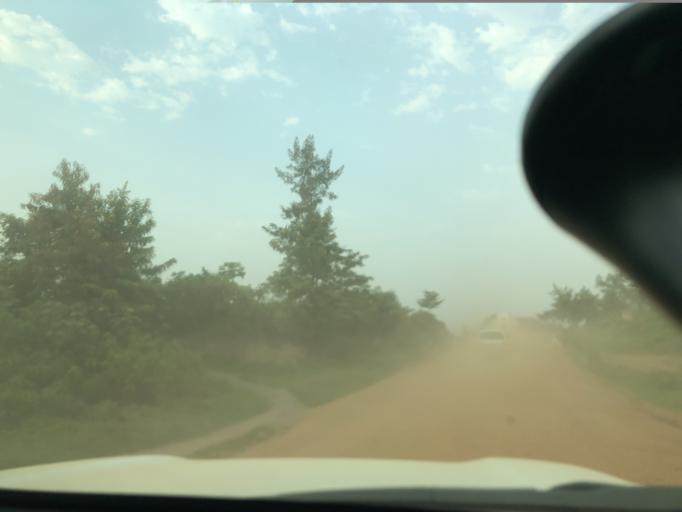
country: UG
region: Western Region
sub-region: Kasese District
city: Margherita
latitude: 0.3246
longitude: 29.6767
